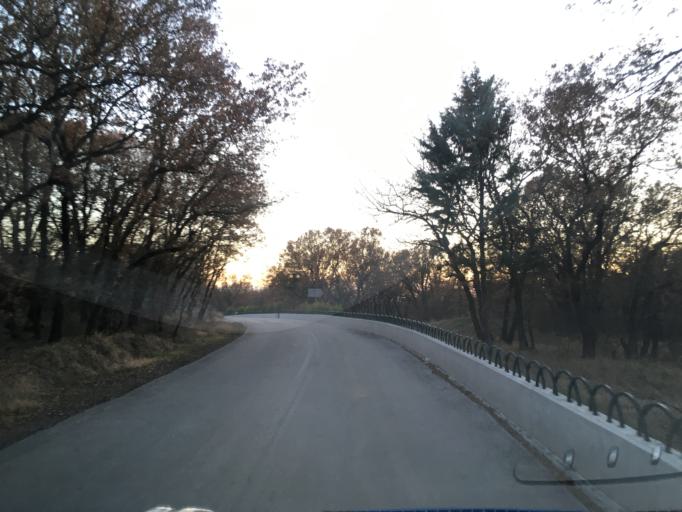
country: GR
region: West Macedonia
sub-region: Nomos Kozanis
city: Koila
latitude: 40.3276
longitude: 21.8319
